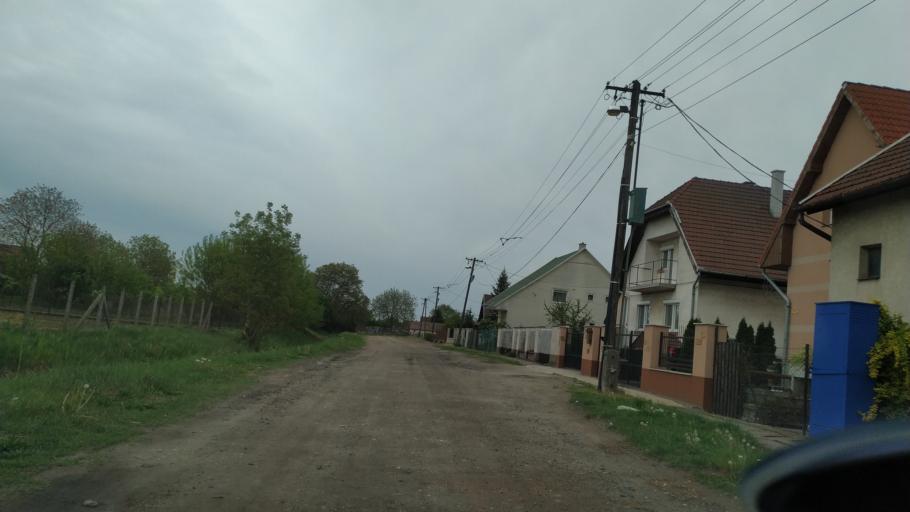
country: HU
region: Pest
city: Nagykata
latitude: 47.4138
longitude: 19.7262
